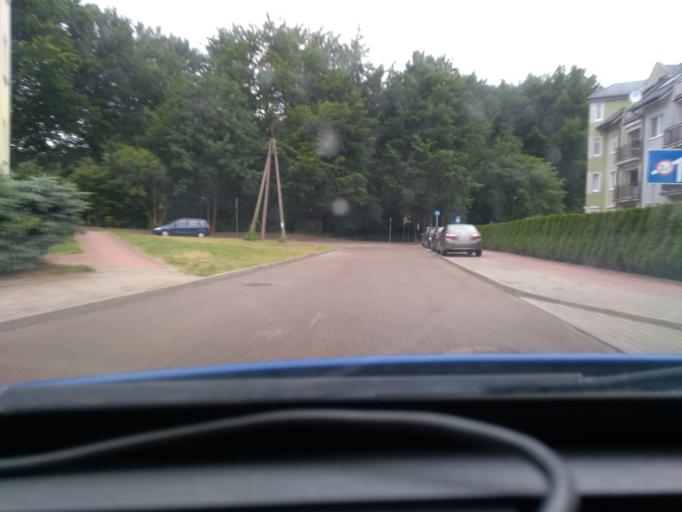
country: PL
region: Pomeranian Voivodeship
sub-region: Powiat kartuski
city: Kartuzy
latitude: 54.3425
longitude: 18.2029
